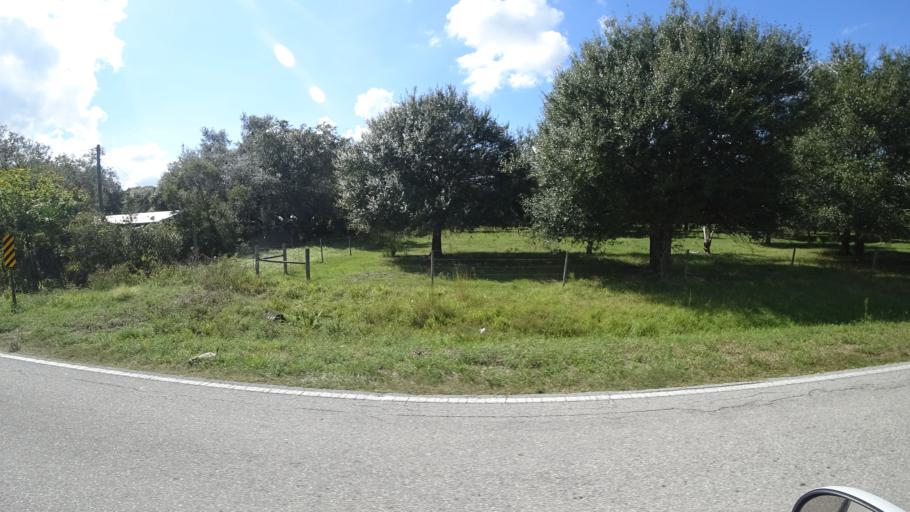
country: US
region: Florida
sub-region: Sarasota County
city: Lake Sarasota
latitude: 27.3537
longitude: -82.1625
